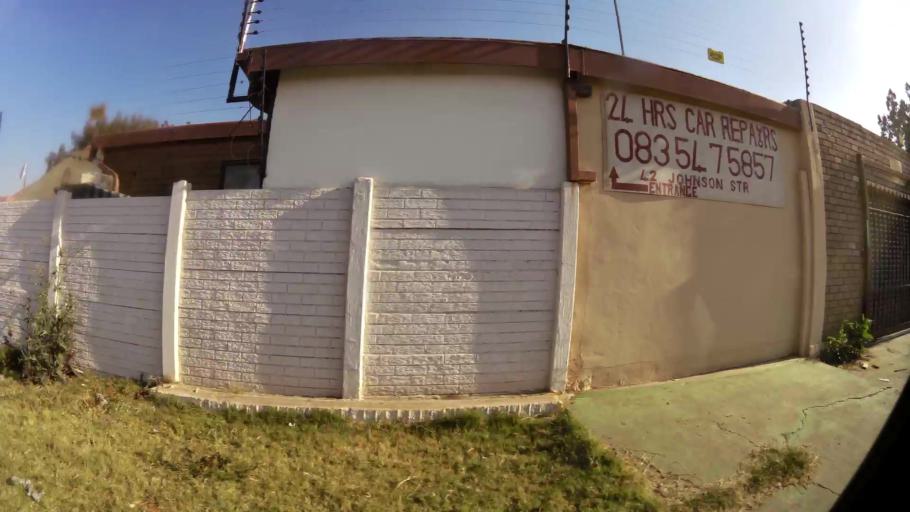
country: ZA
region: North-West
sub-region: Bojanala Platinum District Municipality
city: Rustenburg
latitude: -25.6499
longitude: 27.2378
